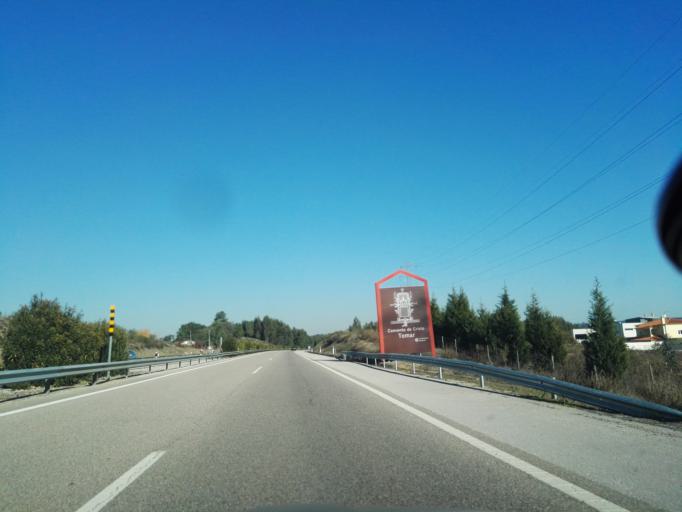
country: PT
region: Santarem
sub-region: Entroncamento
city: Entroncamento
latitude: 39.4821
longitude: -8.4775
